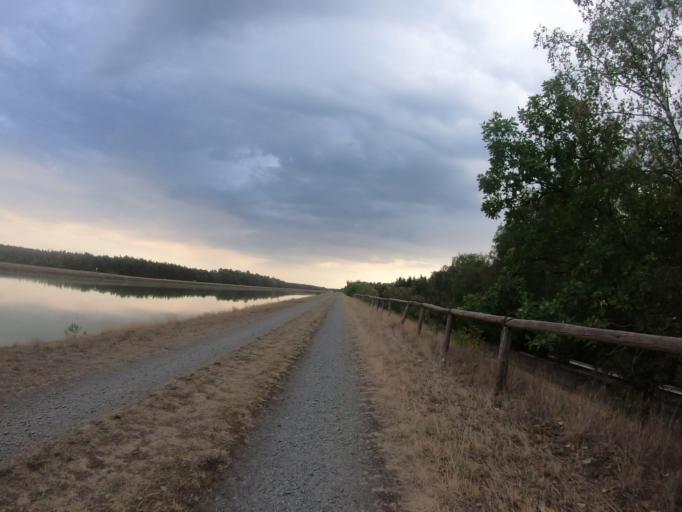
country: DE
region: Lower Saxony
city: Sassenburg
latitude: 52.5537
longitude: 10.6602
